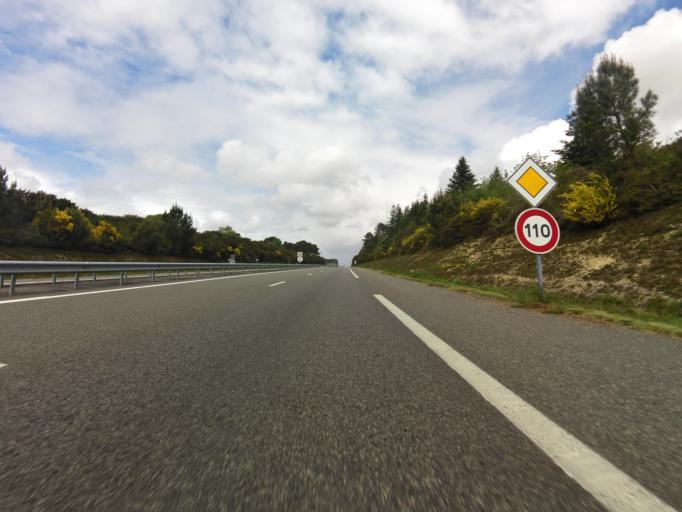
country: FR
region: Brittany
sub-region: Departement du Morbihan
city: Allaire
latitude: 47.6151
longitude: -2.1512
